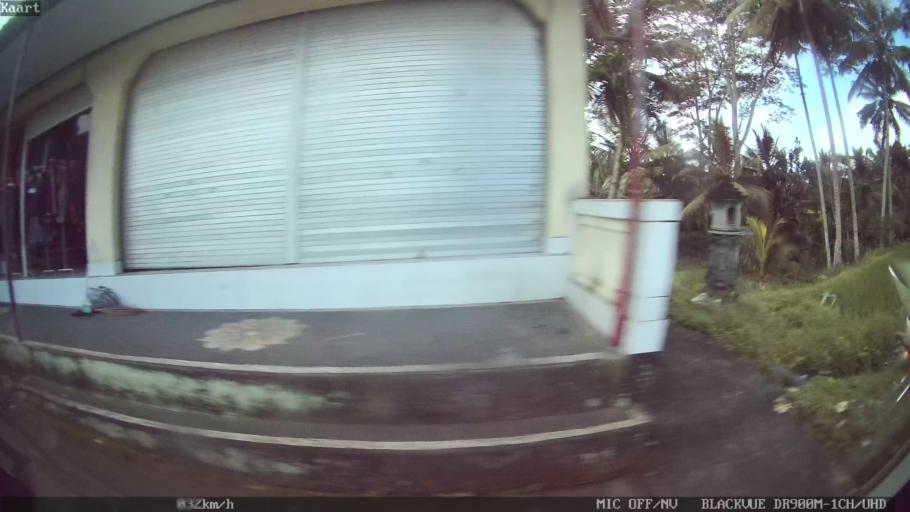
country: ID
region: Bali
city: Banjar Petak
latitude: -8.4545
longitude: 115.3188
